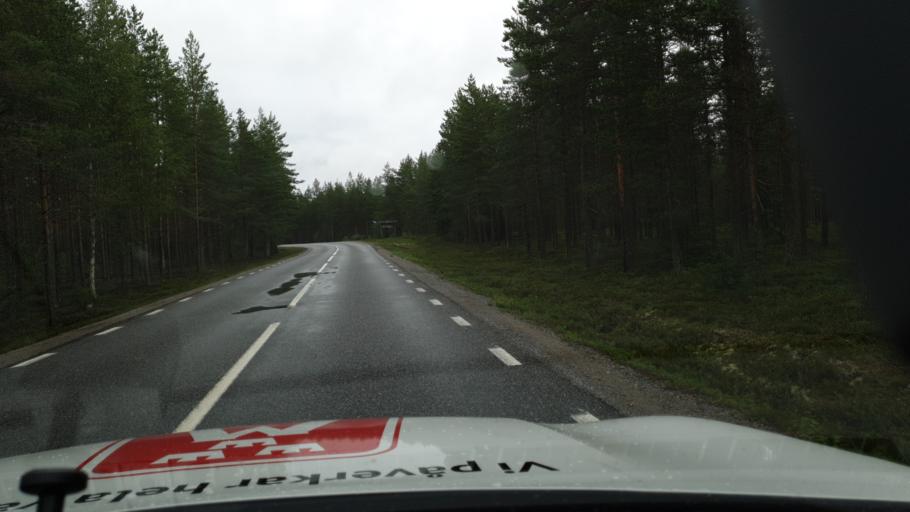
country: SE
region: Vaesterbotten
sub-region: Umea Kommun
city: Saevar
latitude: 64.0159
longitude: 20.4892
